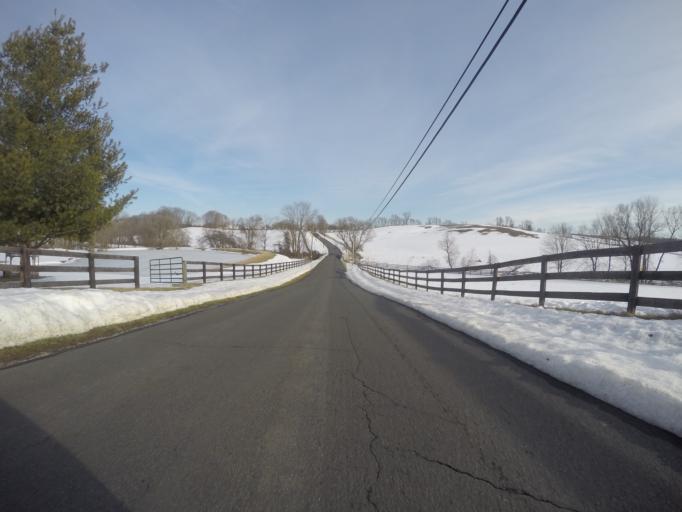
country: US
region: Maryland
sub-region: Baltimore County
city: Hunt Valley
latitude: 39.5545
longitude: -76.5958
